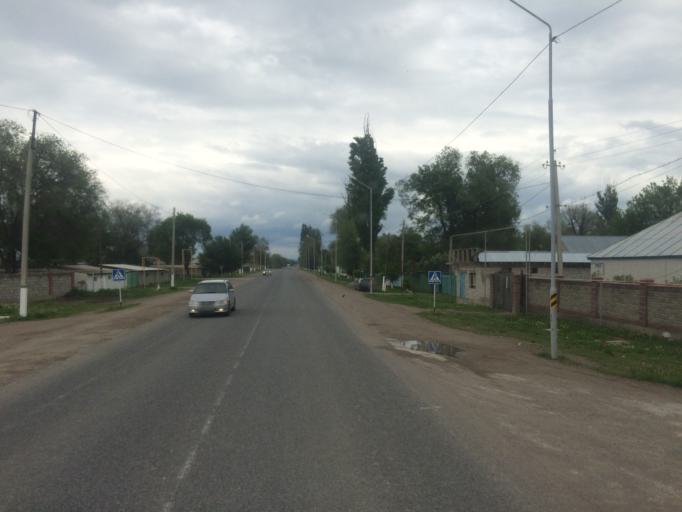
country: KZ
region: Zhambyl
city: Georgiyevka
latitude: 43.2273
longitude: 74.3942
